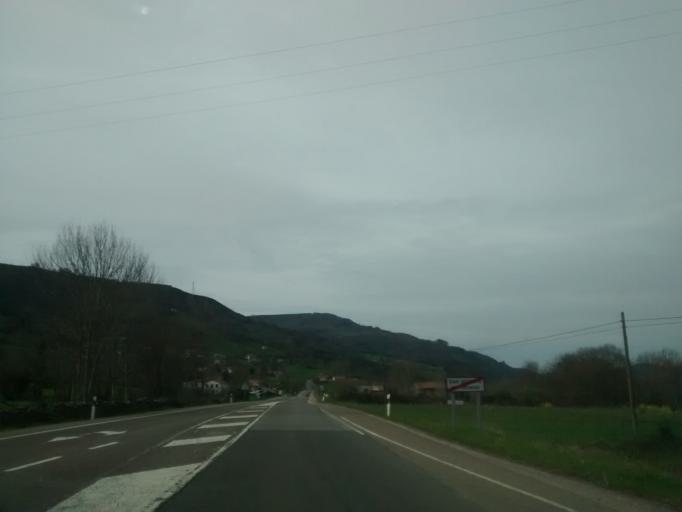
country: ES
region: Cantabria
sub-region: Provincia de Cantabria
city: Santiurde de Toranzo
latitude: 43.2162
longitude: -3.9416
